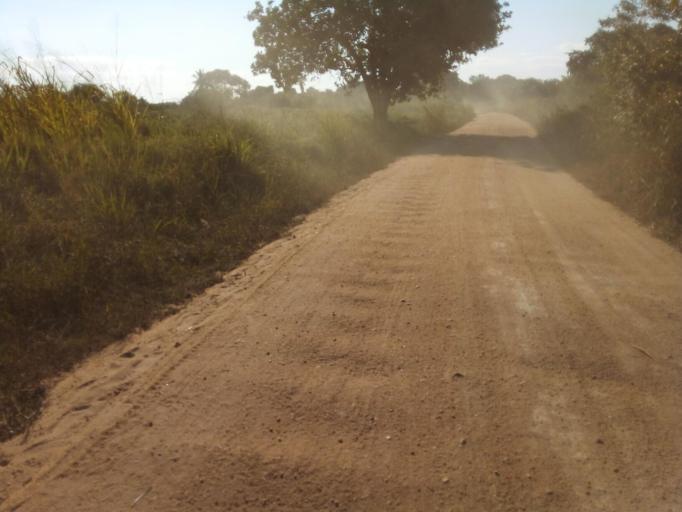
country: MZ
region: Zambezia
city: Quelimane
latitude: -17.5410
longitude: 36.6253
